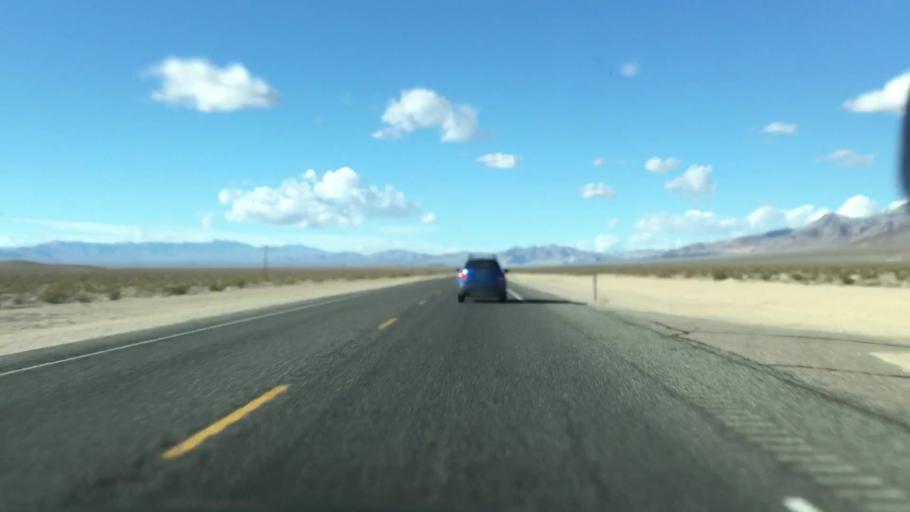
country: US
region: Nevada
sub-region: Nye County
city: Beatty
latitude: 36.7306
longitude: -116.6321
